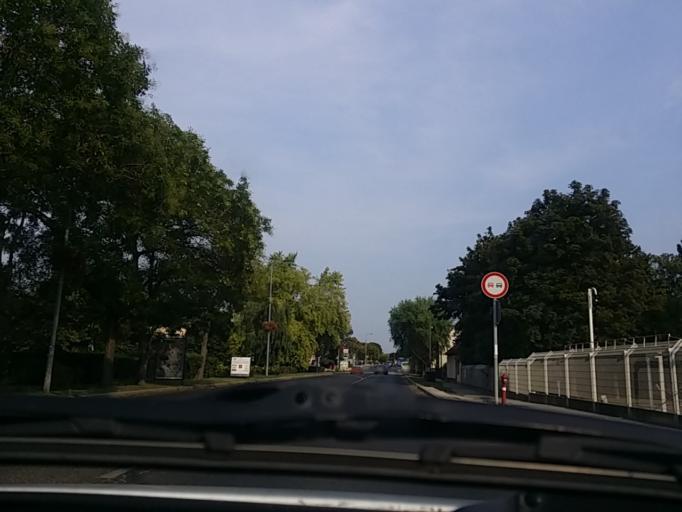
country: HU
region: Pest
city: Budaors
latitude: 47.4613
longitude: 18.9473
